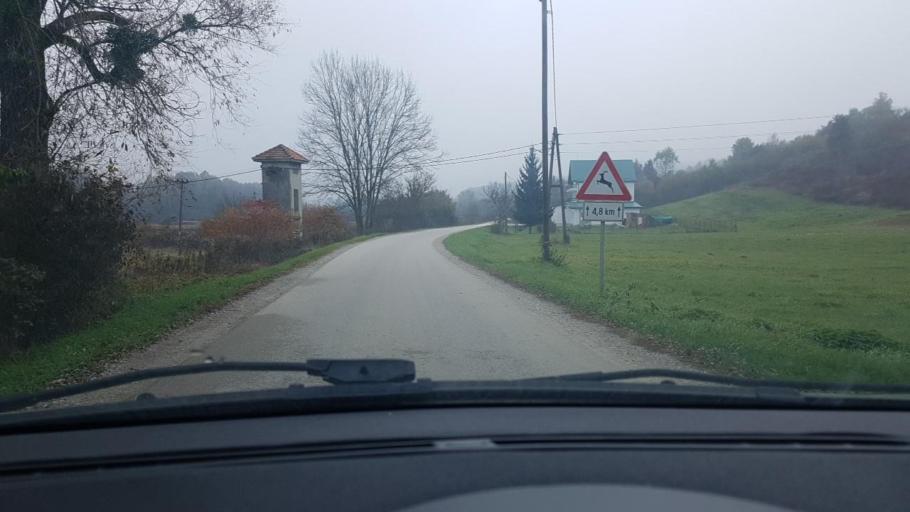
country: HR
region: Krapinsko-Zagorska
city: Zlatar
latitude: 46.0965
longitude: 16.1748
